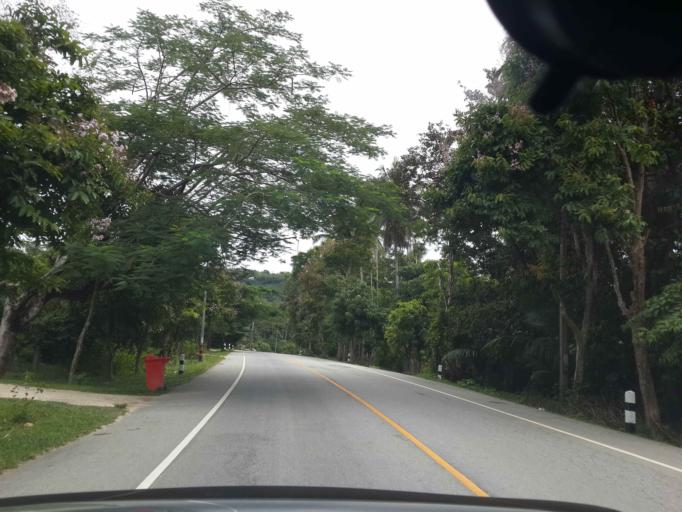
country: TH
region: Narathiwat
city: Rueso
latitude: 6.3624
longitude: 101.5412
